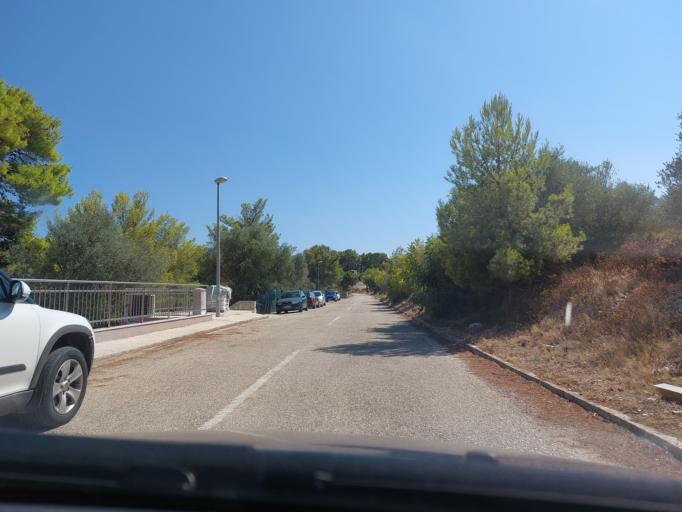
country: HR
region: Dubrovacko-Neretvanska
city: Smokvica
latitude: 42.7340
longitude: 16.8849
